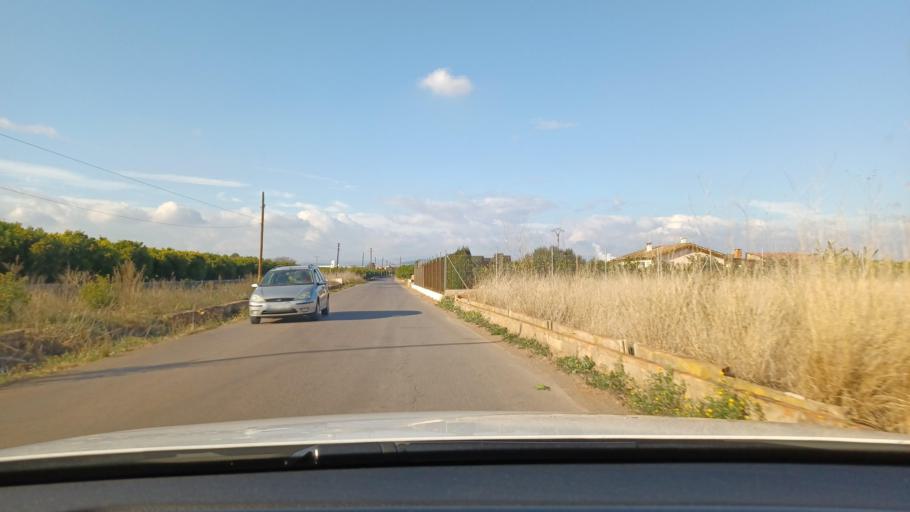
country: ES
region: Valencia
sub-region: Provincia de Castello
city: Betxi
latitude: 39.9366
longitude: -0.2078
